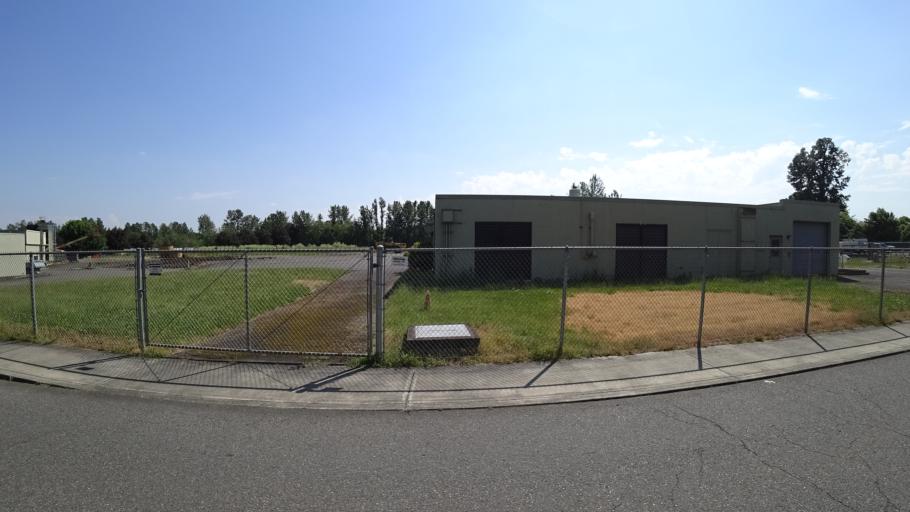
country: US
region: Oregon
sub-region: Multnomah County
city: Lents
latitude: 45.5641
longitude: -122.5403
